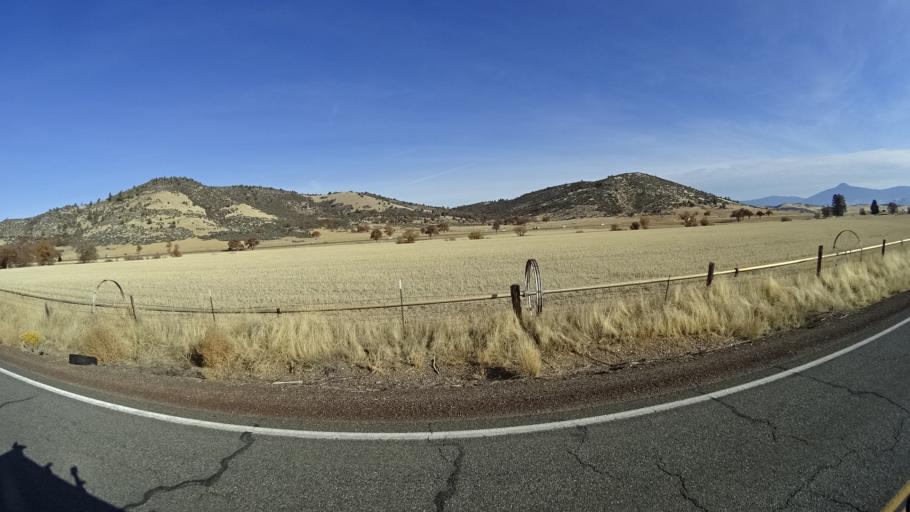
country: US
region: California
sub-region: Siskiyou County
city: Montague
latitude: 41.6568
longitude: -122.5835
